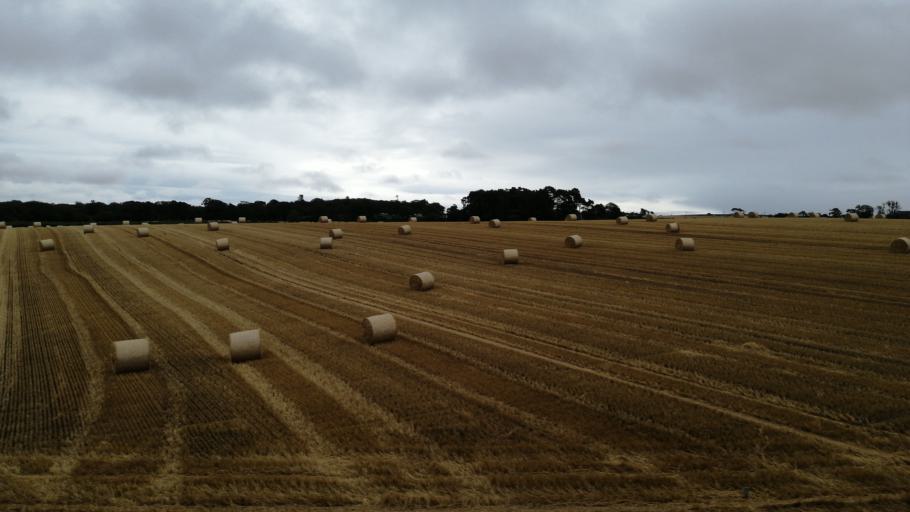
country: GB
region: Scotland
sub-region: Angus
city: Arbroath
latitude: 56.5932
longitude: -2.6024
